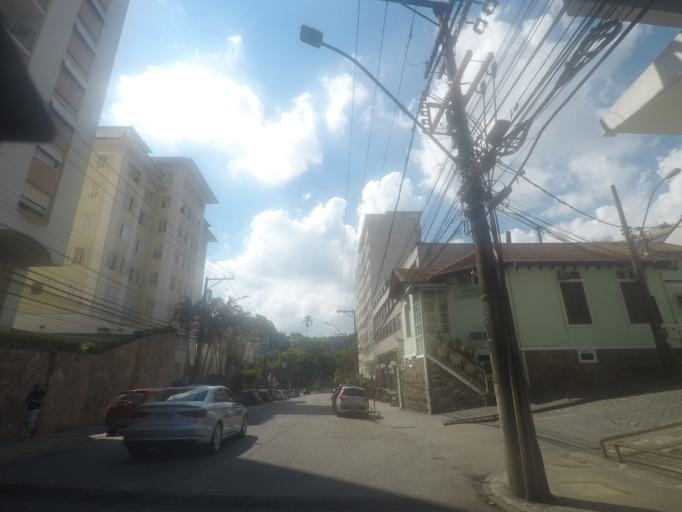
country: BR
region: Rio de Janeiro
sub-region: Petropolis
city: Petropolis
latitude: -22.5112
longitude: -43.1814
